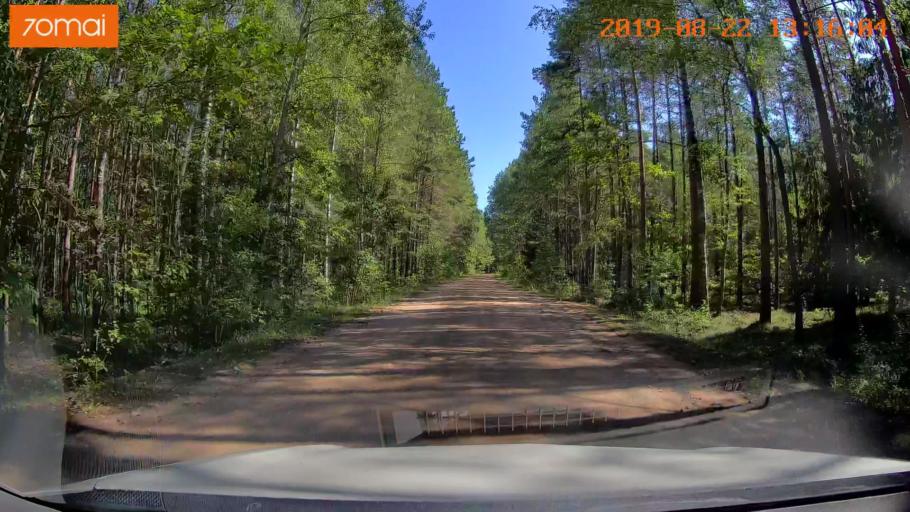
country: BY
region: Minsk
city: Prawdzinski
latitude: 53.2573
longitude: 27.9067
